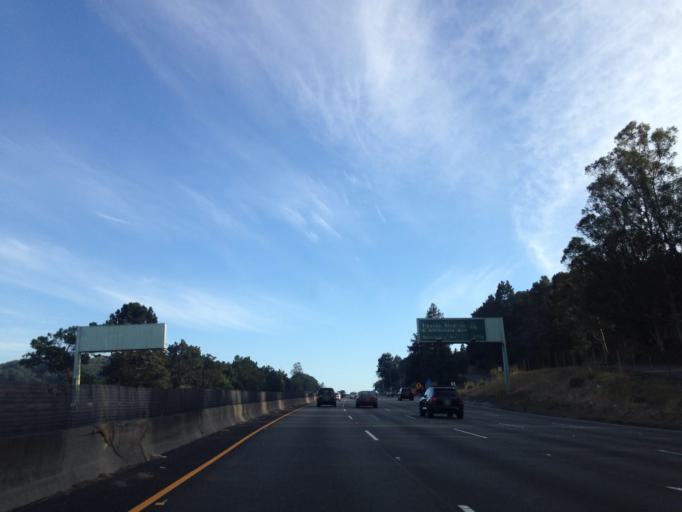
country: US
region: California
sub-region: Marin County
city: Corte Madera
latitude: 37.9167
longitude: -122.5113
